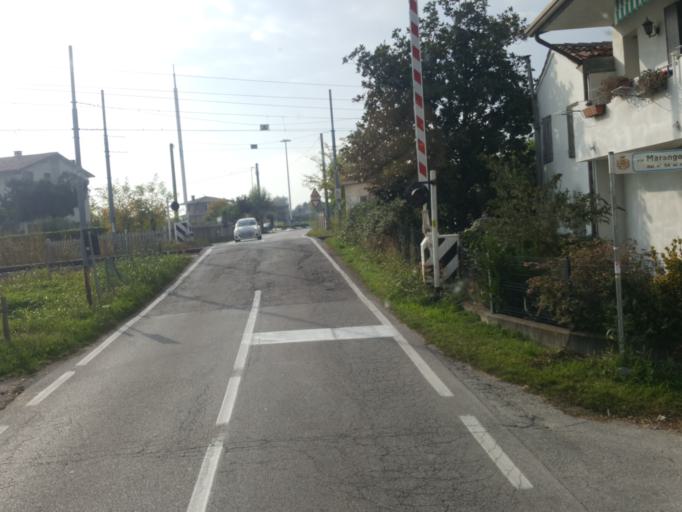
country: IT
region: Veneto
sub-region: Provincia di Vicenza
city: Rossano Veneto
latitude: 45.7184
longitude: 11.8227
